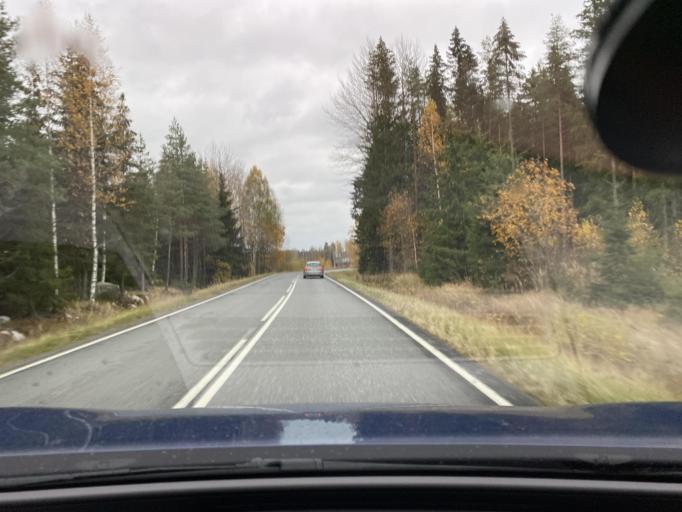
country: FI
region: Satakunta
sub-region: Pori
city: Huittinen
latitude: 61.1223
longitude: 22.5786
